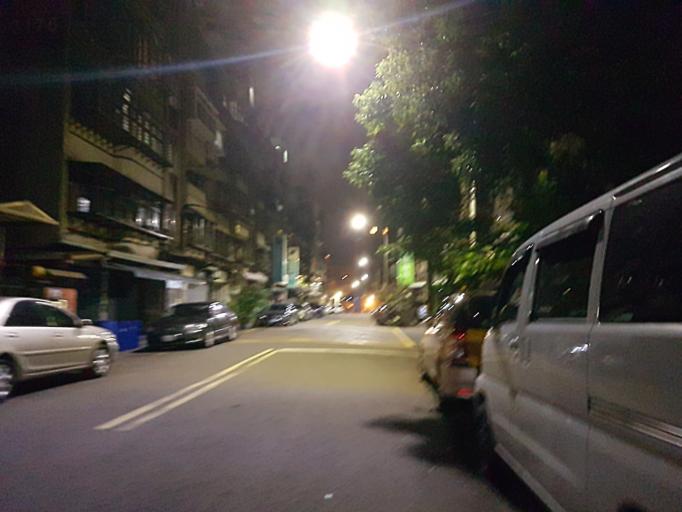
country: TW
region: Taipei
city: Taipei
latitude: 25.0005
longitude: 121.5377
